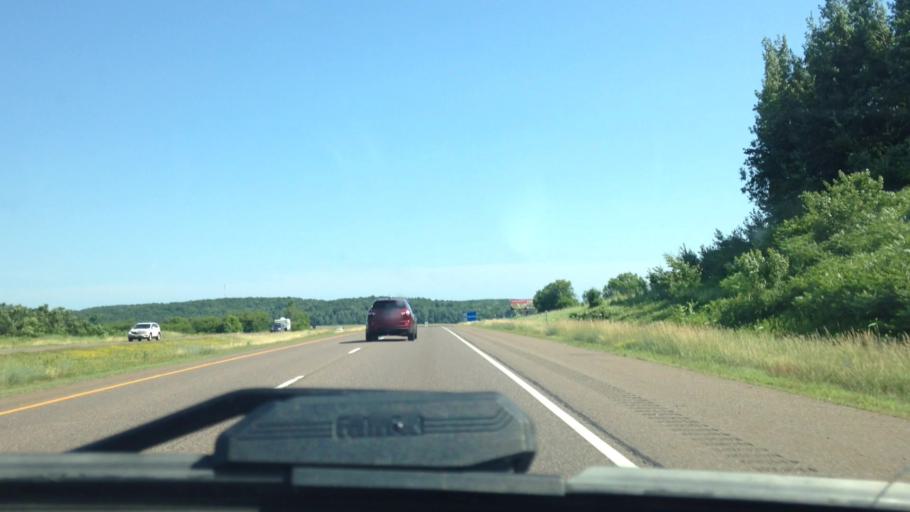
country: US
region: Wisconsin
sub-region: Chippewa County
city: Chippewa Falls
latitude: 44.9551
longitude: -91.4256
